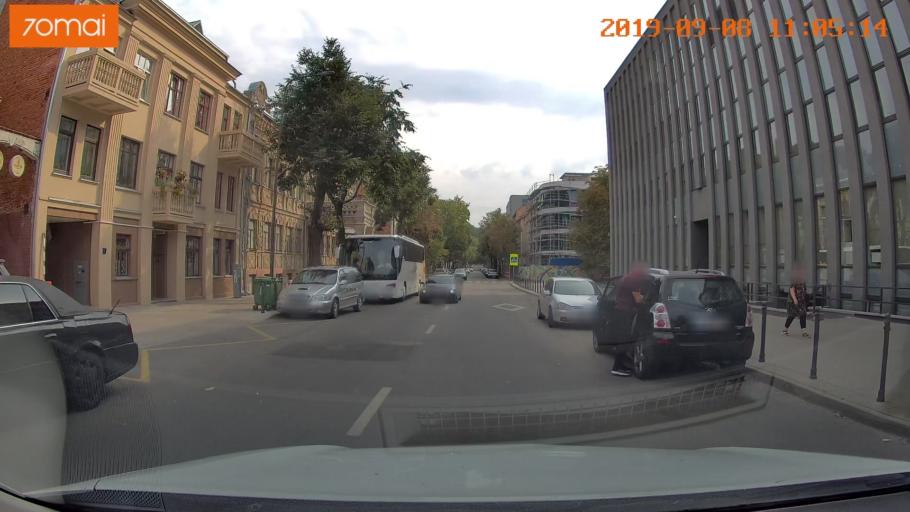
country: LT
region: Kauno apskritis
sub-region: Kaunas
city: Kaunas
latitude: 54.9006
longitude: 23.9134
